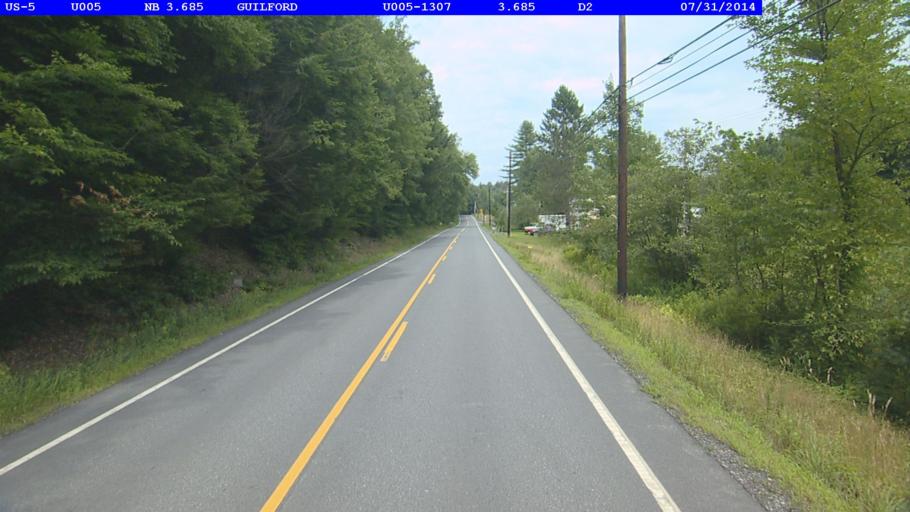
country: US
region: Vermont
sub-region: Windham County
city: Brattleboro
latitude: 42.7815
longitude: -72.5700
